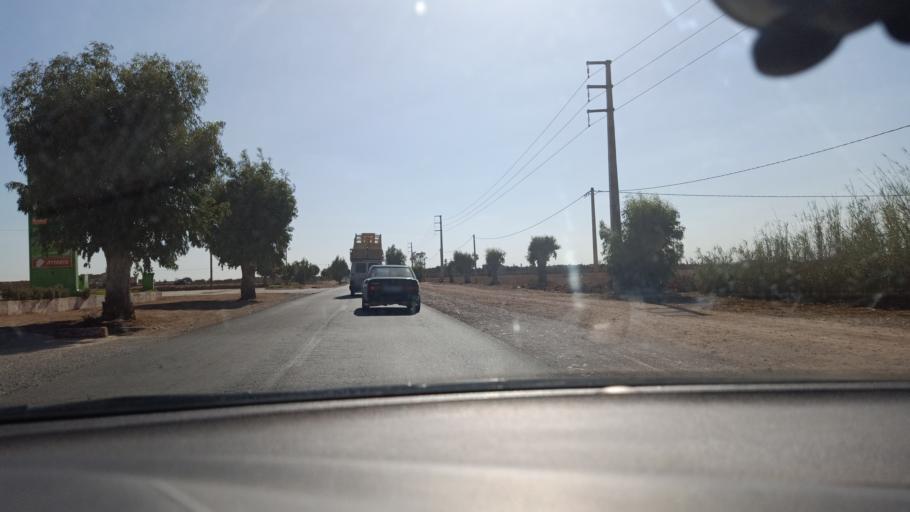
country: MA
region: Doukkala-Abda
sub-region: Safi
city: Youssoufia
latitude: 32.0982
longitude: -8.6139
